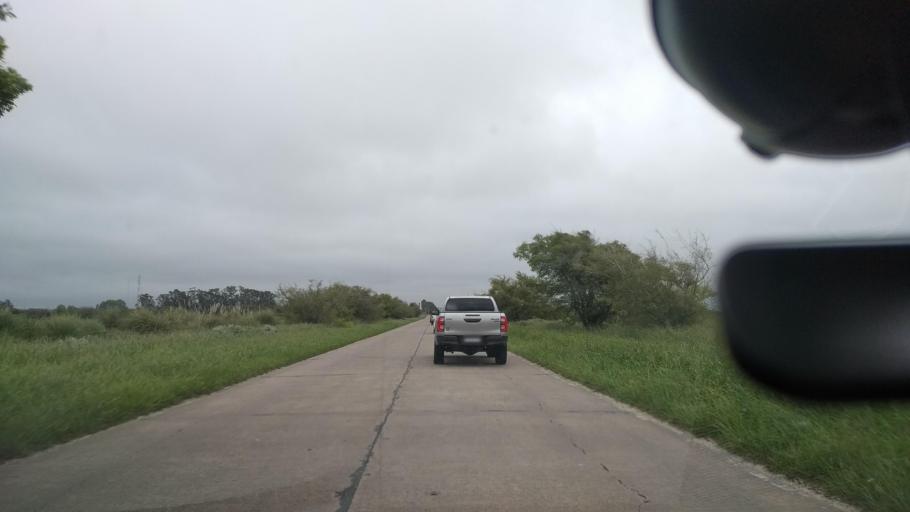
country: AR
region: Buenos Aires
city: Veronica
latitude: -35.5396
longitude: -57.3171
